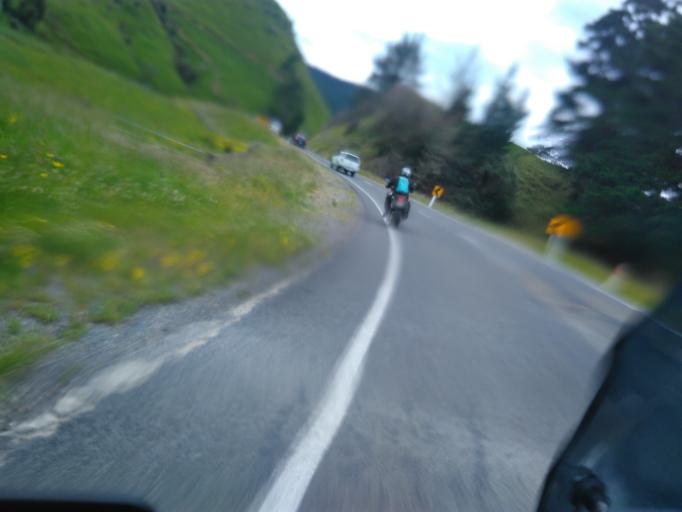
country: NZ
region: Bay of Plenty
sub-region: Opotiki District
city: Opotiki
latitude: -38.3741
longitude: 177.4647
